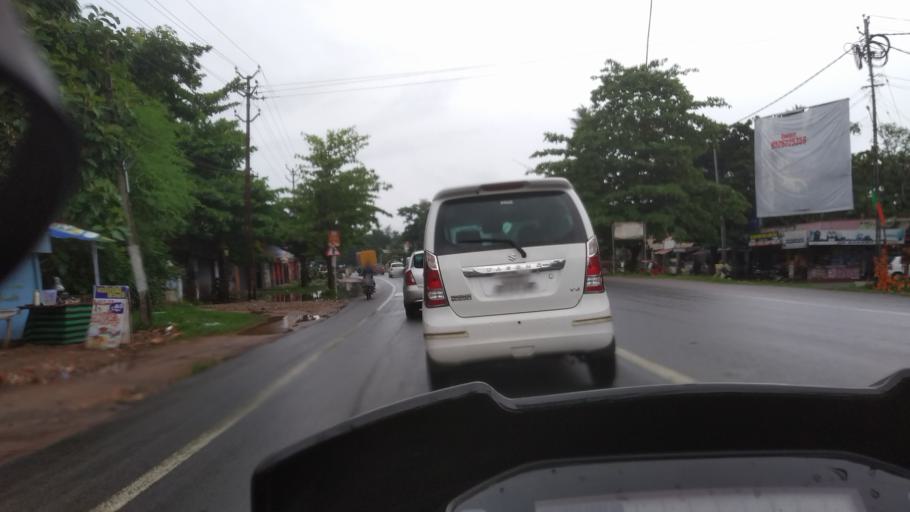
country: IN
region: Kerala
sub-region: Alappuzha
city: Kayankulam
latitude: 9.1254
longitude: 76.5171
